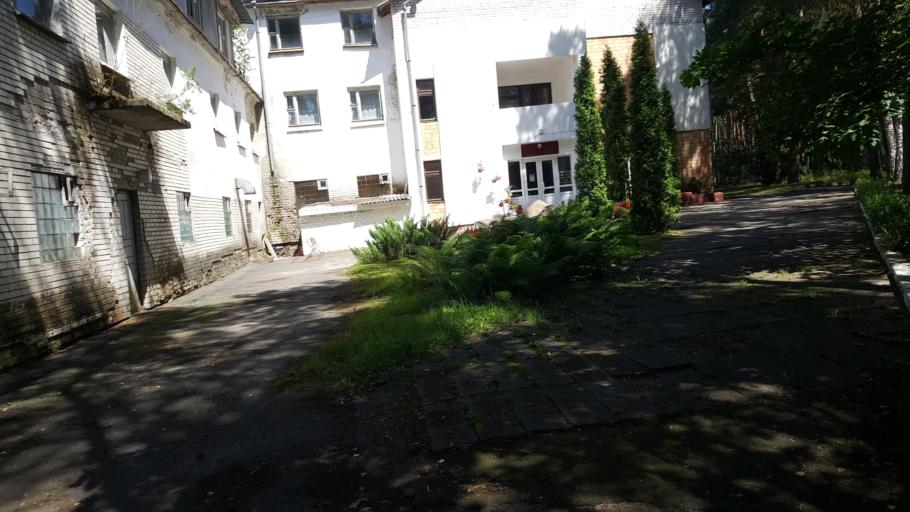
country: BY
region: Brest
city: Kamyanyets
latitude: 52.3279
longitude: 23.9016
